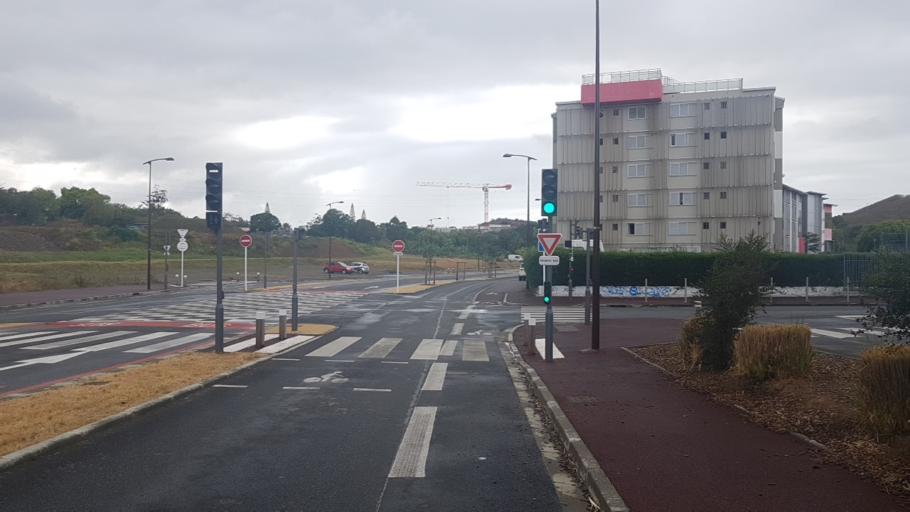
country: NC
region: South Province
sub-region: Noumea
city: Noumea
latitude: -22.2197
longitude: 166.4747
